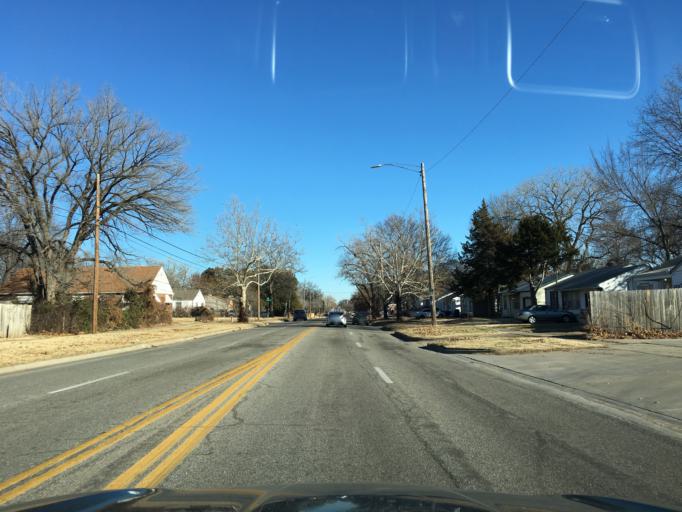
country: US
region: Kansas
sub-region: Sedgwick County
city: Wichita
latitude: 37.6719
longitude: -97.2703
